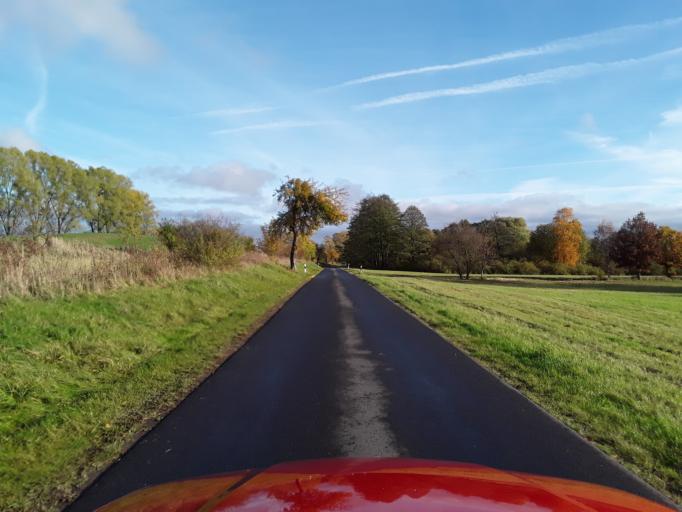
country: DE
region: Brandenburg
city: Mittenwalde
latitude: 53.2628
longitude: 13.7212
